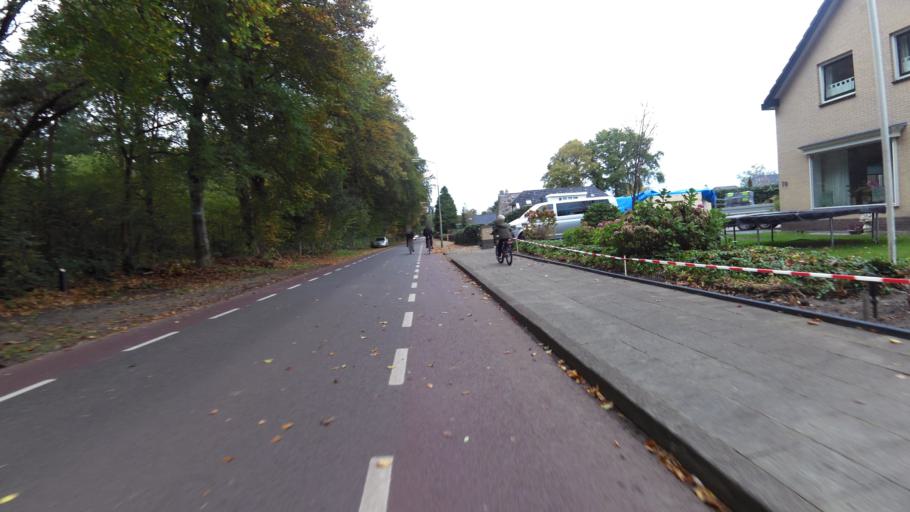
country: NL
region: Gelderland
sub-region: Gemeente Oldebroek
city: Oldebroek
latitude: 52.4422
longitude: 5.9532
